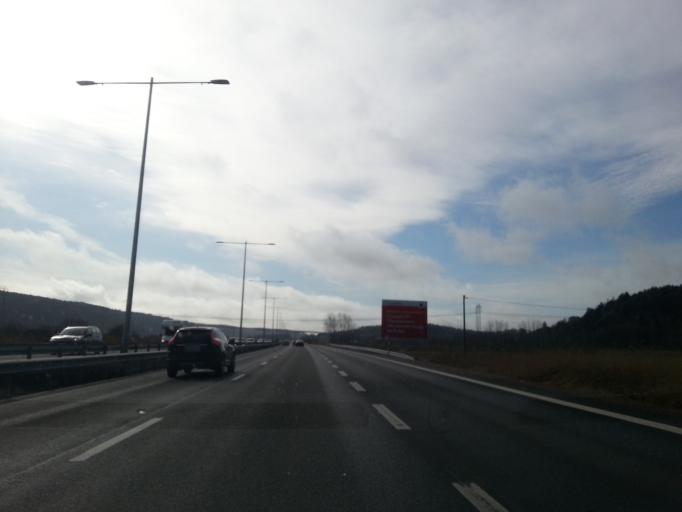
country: SE
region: Vaestra Goetaland
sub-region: Ale Kommun
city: Surte
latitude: 57.8210
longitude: 12.0044
